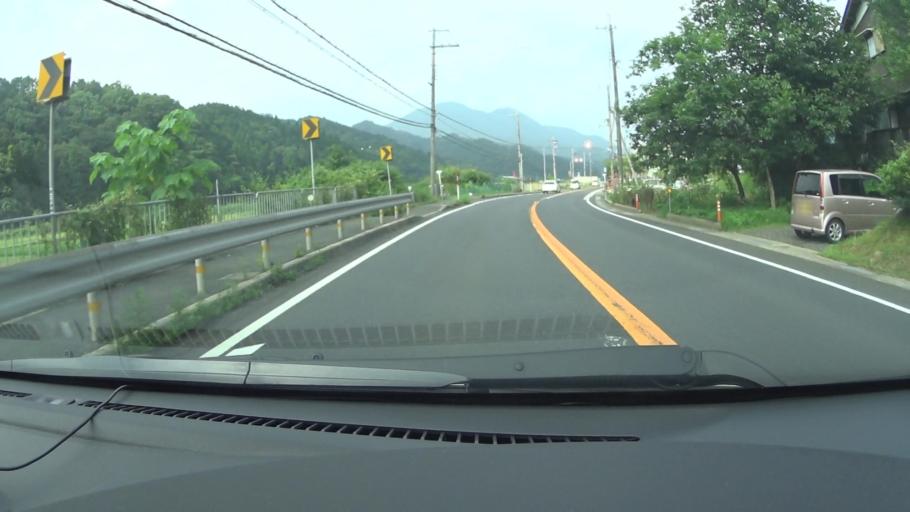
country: JP
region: Kyoto
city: Maizuru
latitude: 35.4823
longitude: 135.4443
